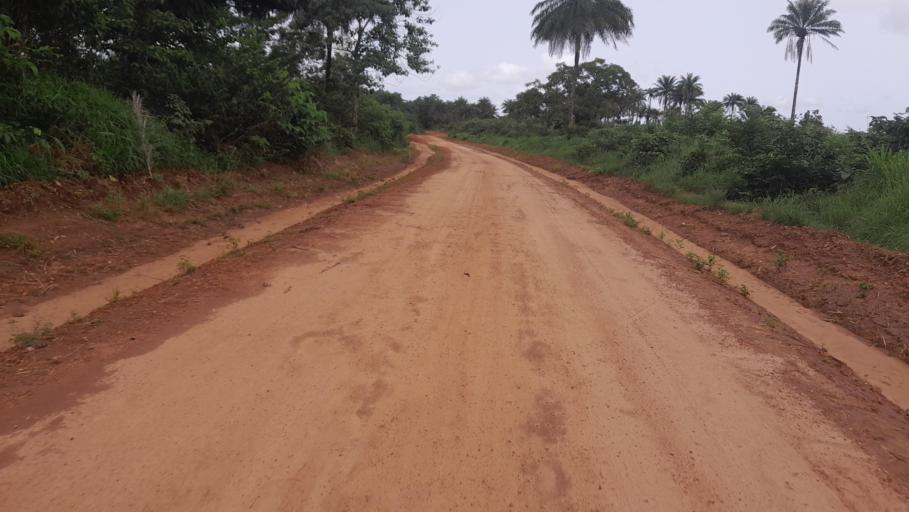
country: GN
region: Boke
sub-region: Boffa
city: Boffa
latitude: 10.0572
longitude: -13.8697
